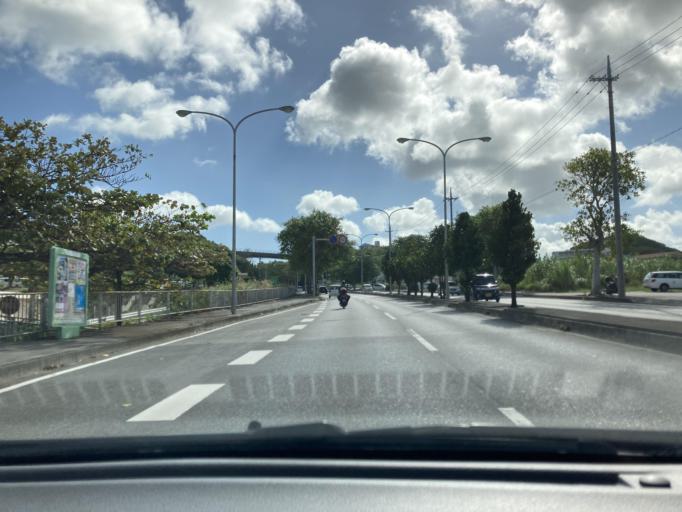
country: JP
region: Okinawa
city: Tomigusuku
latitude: 26.1782
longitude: 127.7144
